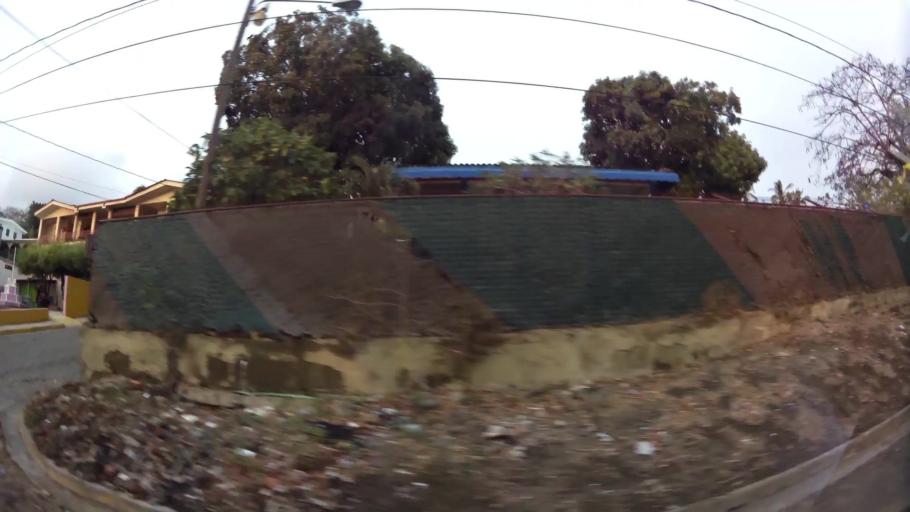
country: NI
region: Rivas
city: San Juan del Sur
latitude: 11.2559
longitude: -85.8718
